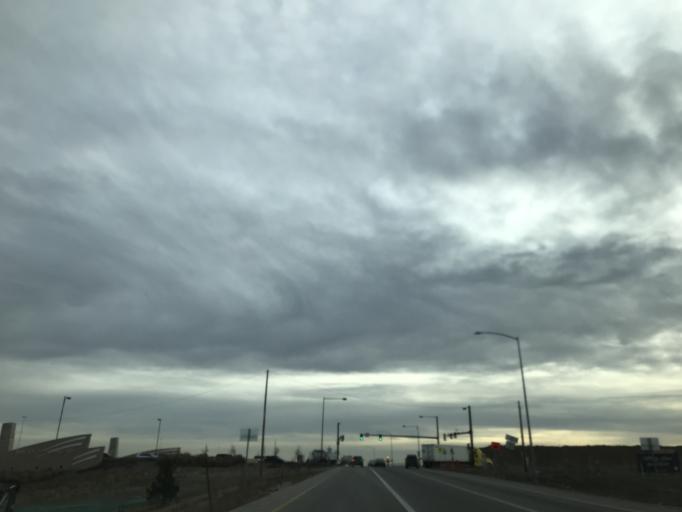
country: US
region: Colorado
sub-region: Adams County
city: Commerce City
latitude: 39.7764
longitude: -104.8844
